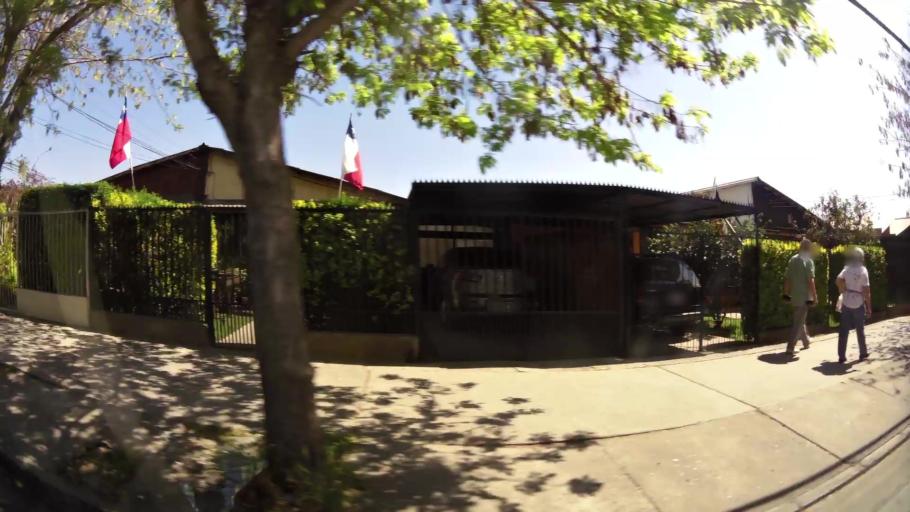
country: CL
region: Santiago Metropolitan
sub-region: Provincia de Santiago
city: Lo Prado
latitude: -33.4939
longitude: -70.7436
